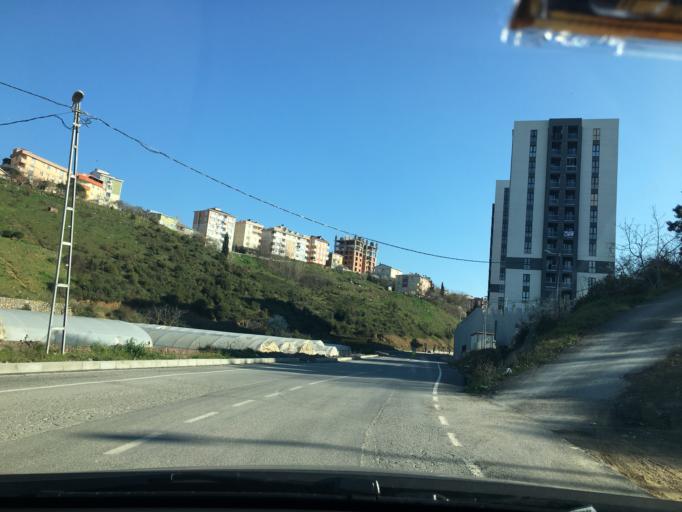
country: TR
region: Istanbul
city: Icmeler
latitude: 40.8726
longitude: 29.3008
